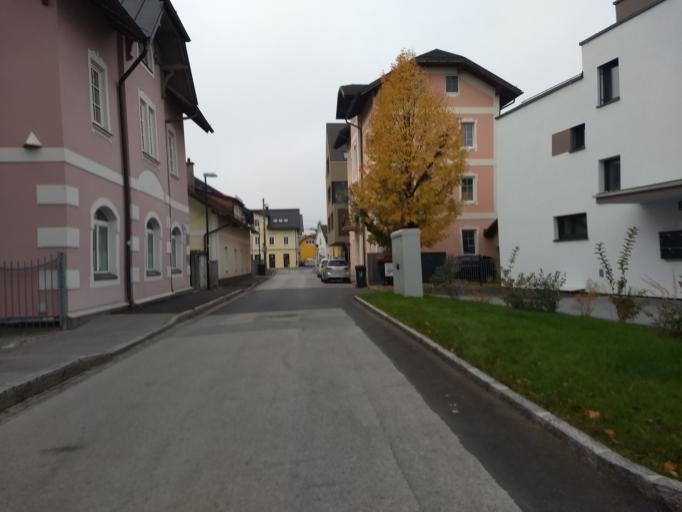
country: AT
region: Salzburg
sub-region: Salzburg Stadt
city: Salzburg
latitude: 47.7982
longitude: 13.0213
